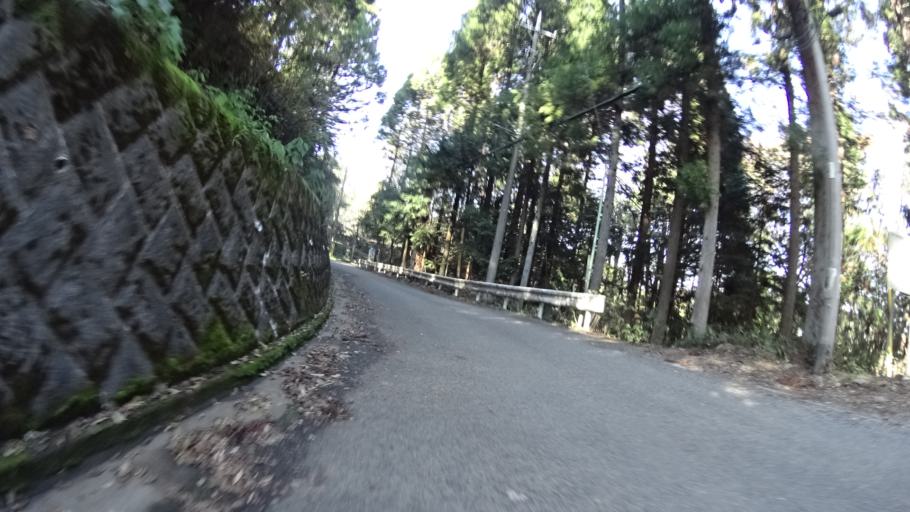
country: JP
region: Kanagawa
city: Zama
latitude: 35.5275
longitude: 139.2731
